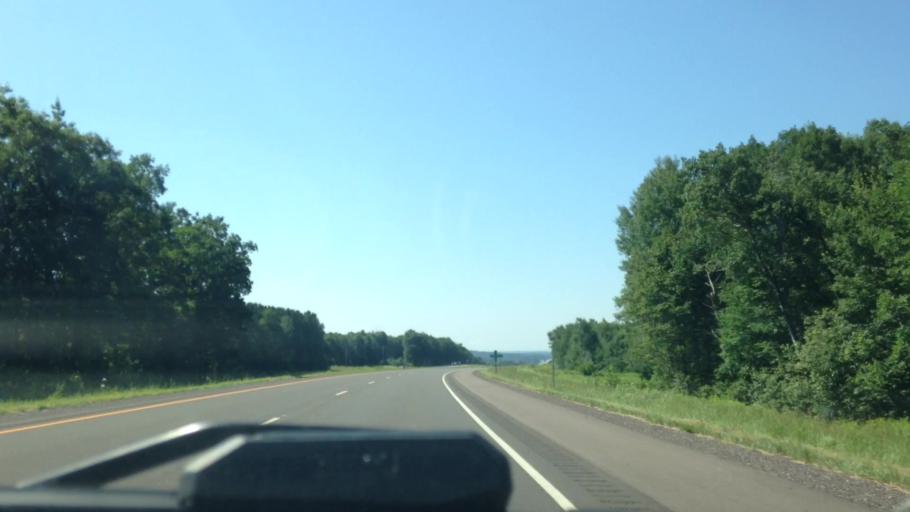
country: US
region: Wisconsin
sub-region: Washburn County
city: Spooner
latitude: 45.9397
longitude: -91.8284
